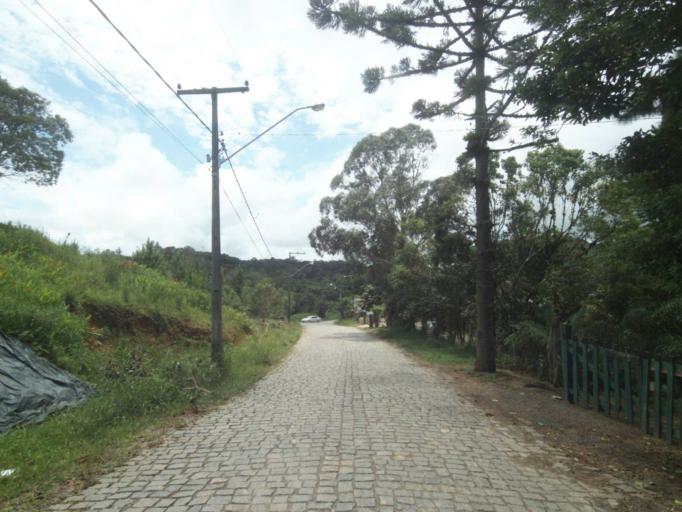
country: BR
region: Parana
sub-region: Campina Grande Do Sul
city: Campina Grande do Sul
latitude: -25.1079
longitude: -48.8068
